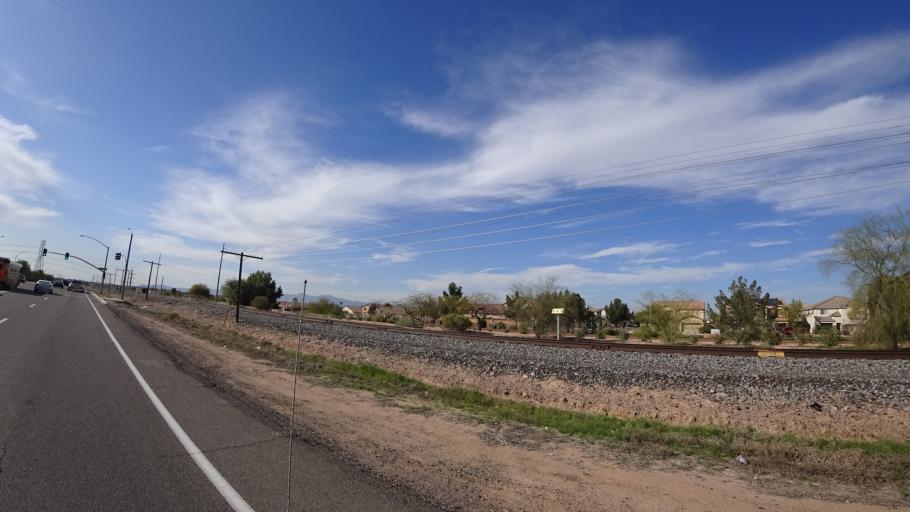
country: US
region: Arizona
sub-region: Maricopa County
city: Avondale
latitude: 33.4355
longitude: -112.3142
